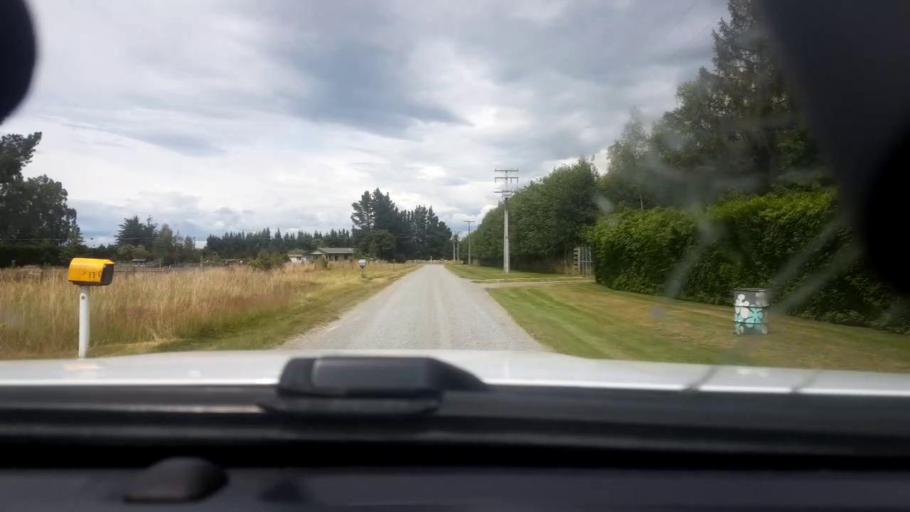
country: NZ
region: Canterbury
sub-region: Timaru District
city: Pleasant Point
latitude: -44.1429
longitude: 171.2891
